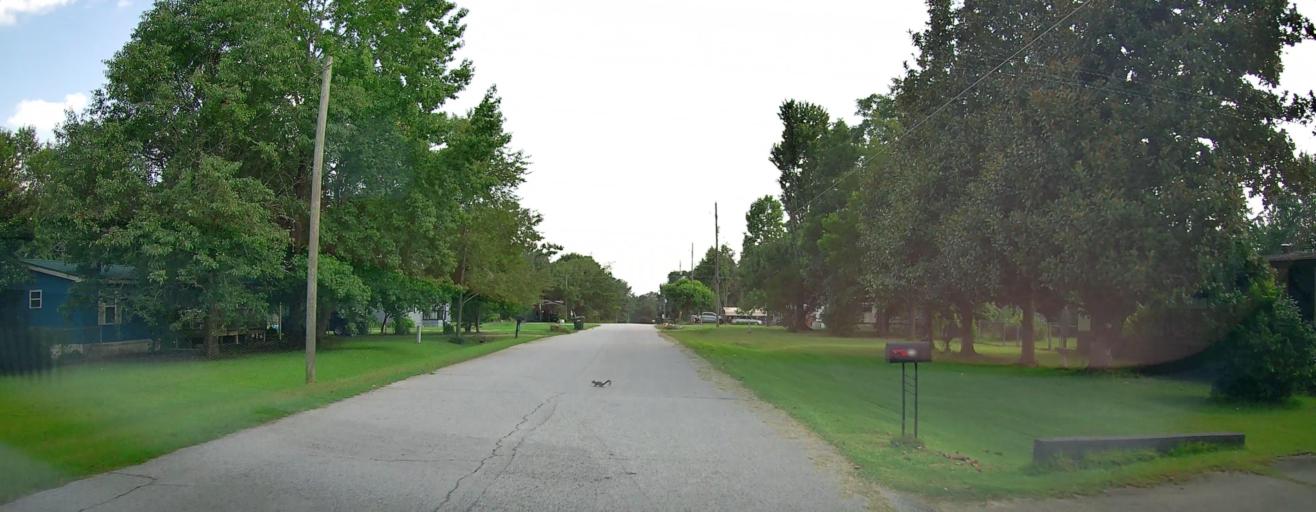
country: US
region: Georgia
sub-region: Houston County
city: Centerville
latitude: 32.6461
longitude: -83.6860
